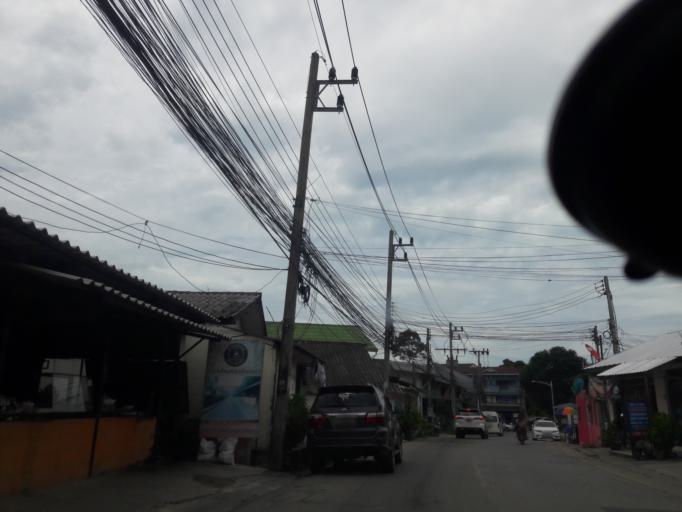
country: TH
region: Surat Thani
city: Ko Samui
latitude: 9.5347
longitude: 100.0445
